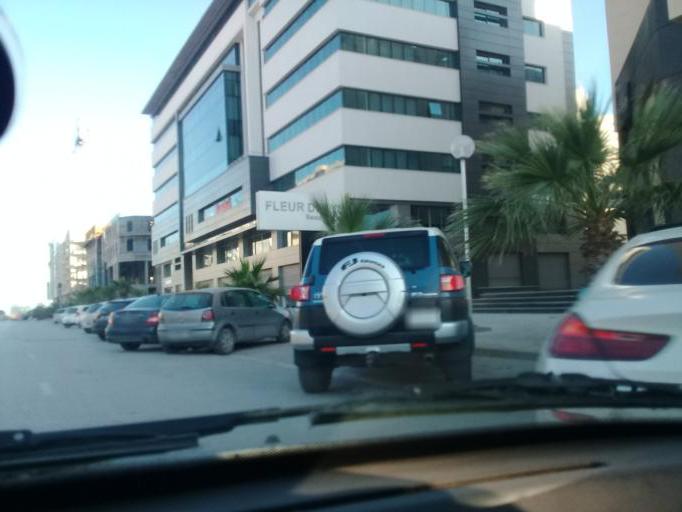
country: TN
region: Tunis
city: La Goulette
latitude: 36.8457
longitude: 10.2804
